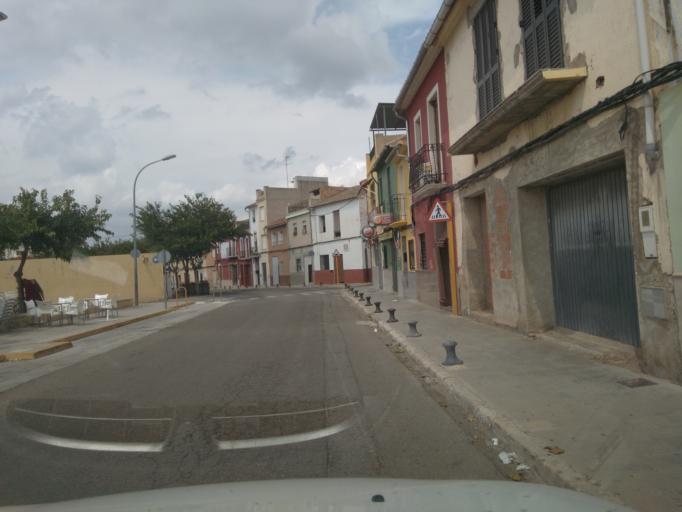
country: ES
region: Valencia
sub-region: Provincia de Valencia
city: Carcaixent
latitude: 39.1156
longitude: -0.4392
